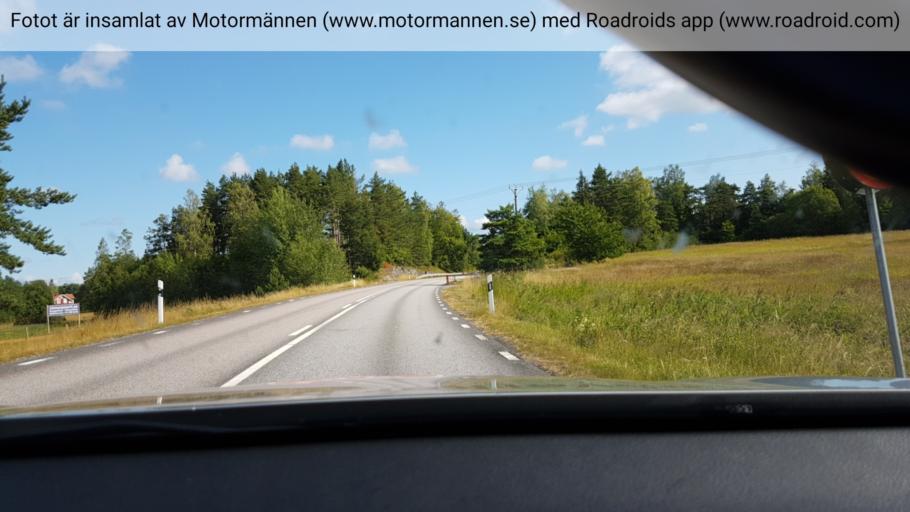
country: SE
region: Stockholm
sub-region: Norrtalje Kommun
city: Norrtalje
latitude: 59.6058
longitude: 18.6738
